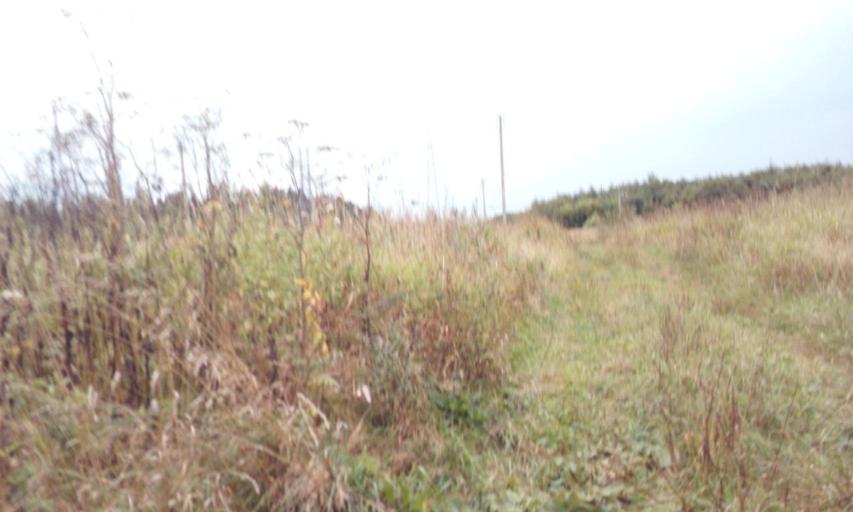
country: RU
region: Moskovskaya
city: Aprelevka
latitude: 55.5788
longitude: 37.0987
